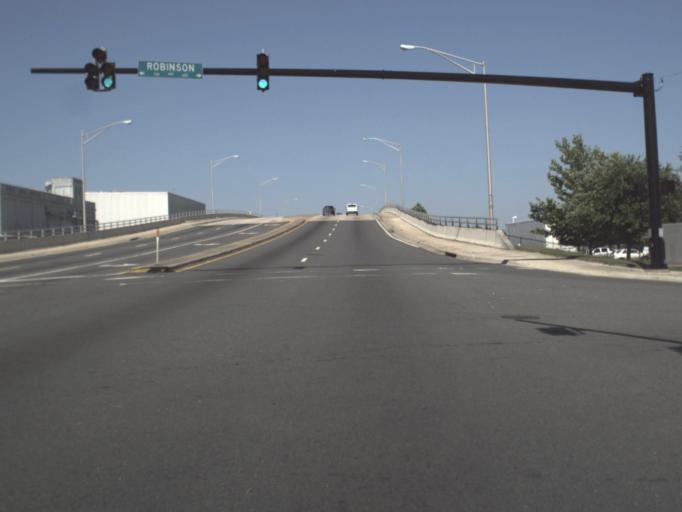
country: US
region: Florida
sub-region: Duval County
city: Jacksonville
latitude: 30.3344
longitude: -81.6884
